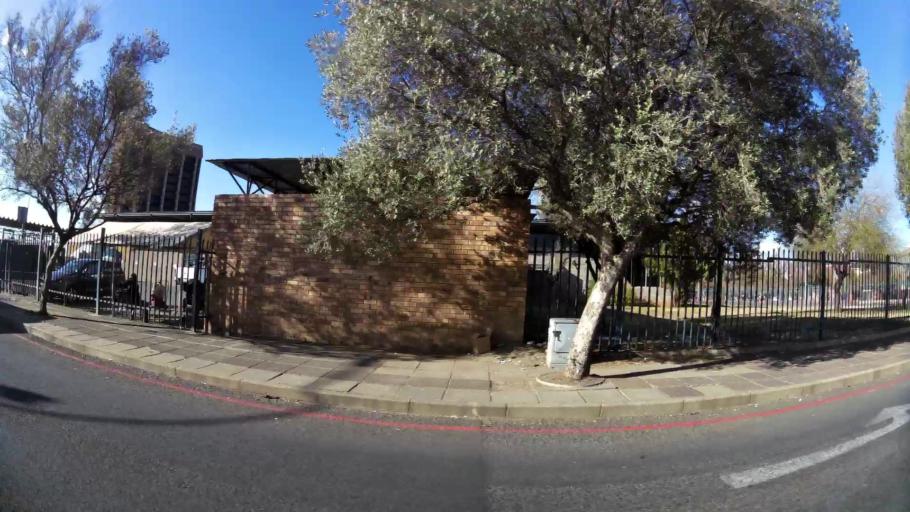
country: ZA
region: Northern Cape
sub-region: Frances Baard District Municipality
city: Kimberley
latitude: -28.7460
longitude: 24.7649
